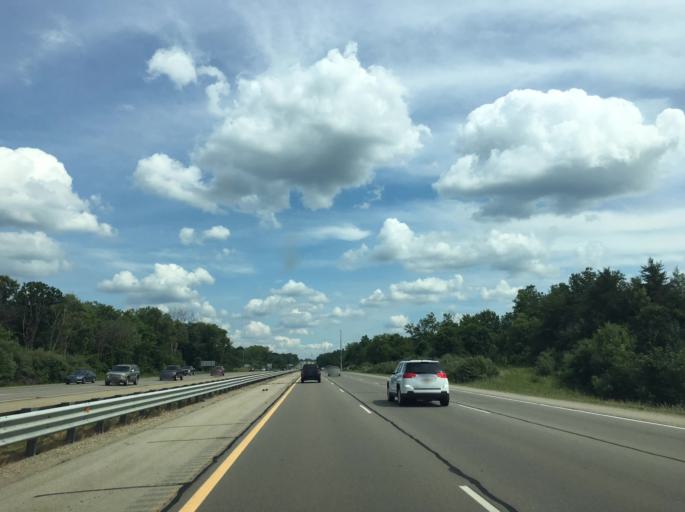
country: US
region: Michigan
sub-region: Oakland County
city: Holly
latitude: 42.8049
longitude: -83.5618
